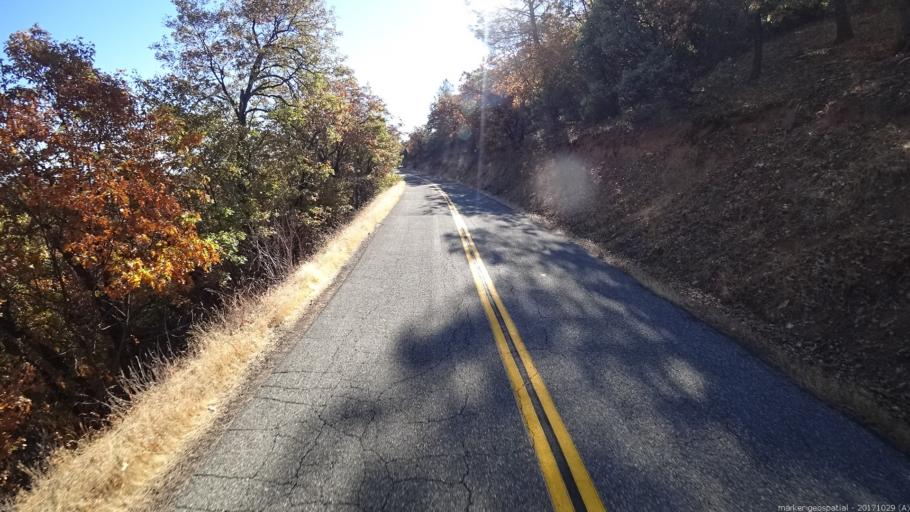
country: US
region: California
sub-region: Trinity County
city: Lewiston
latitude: 40.3679
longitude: -122.8490
